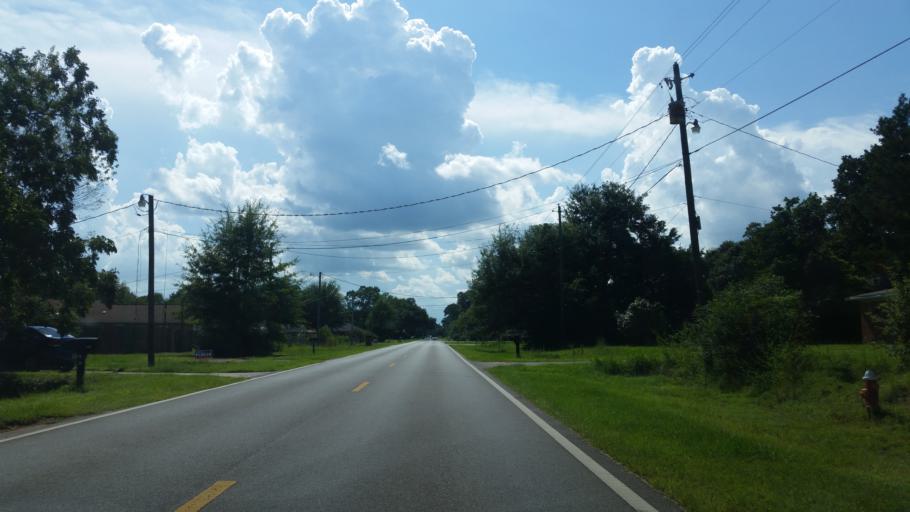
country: US
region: Florida
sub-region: Santa Rosa County
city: Pace
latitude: 30.5896
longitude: -87.1513
